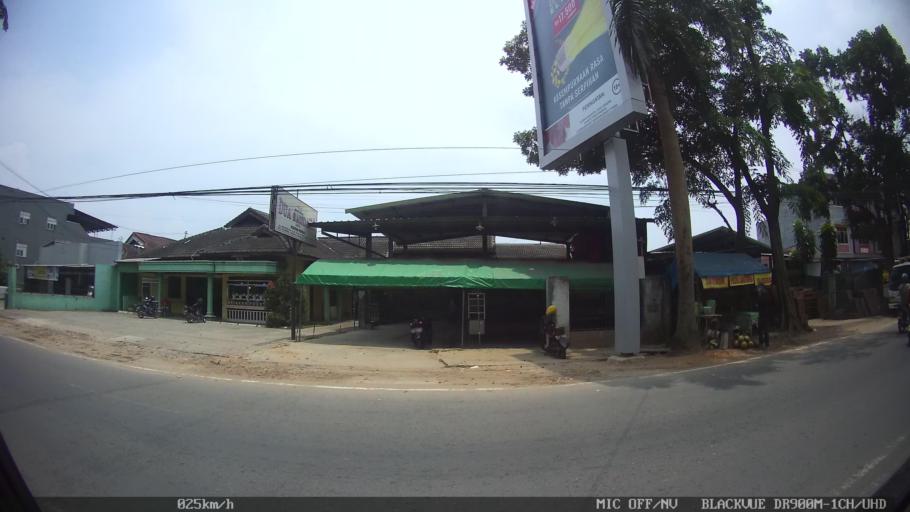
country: ID
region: Lampung
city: Kedaton
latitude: -5.3955
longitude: 105.2922
